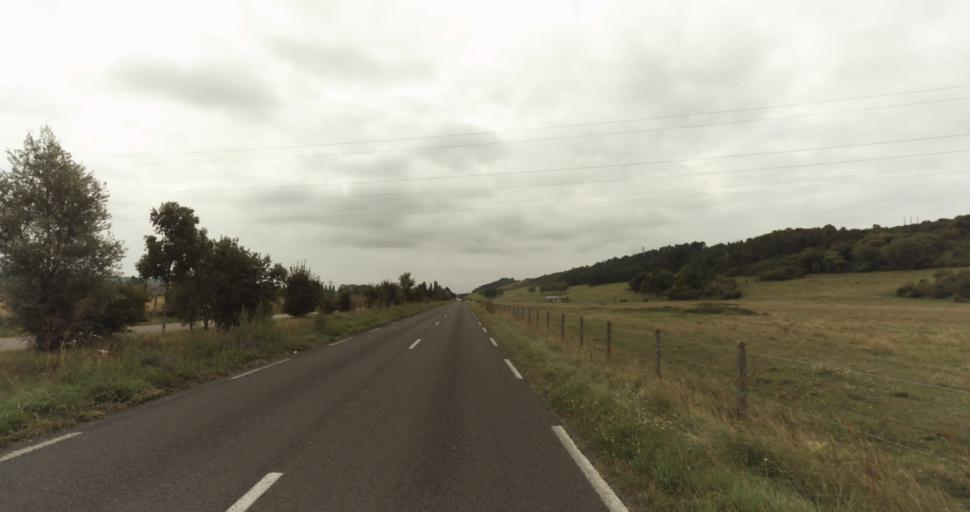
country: FR
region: Haute-Normandie
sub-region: Departement de l'Eure
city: Garennes-sur-Eure
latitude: 48.9048
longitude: 1.4459
